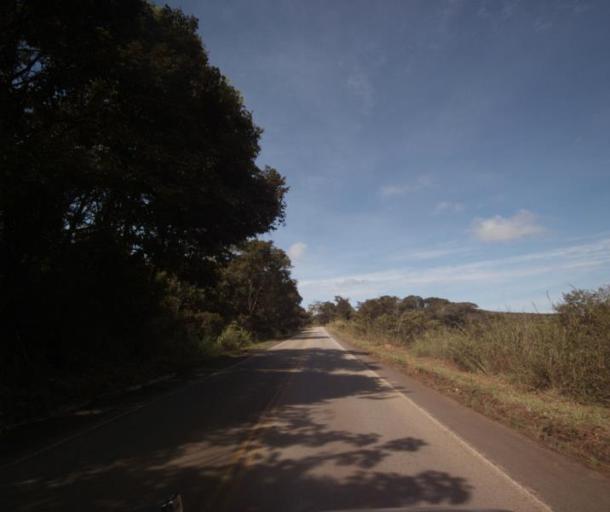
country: BR
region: Goias
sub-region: Abadiania
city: Abadiania
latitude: -16.1253
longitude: -48.8947
